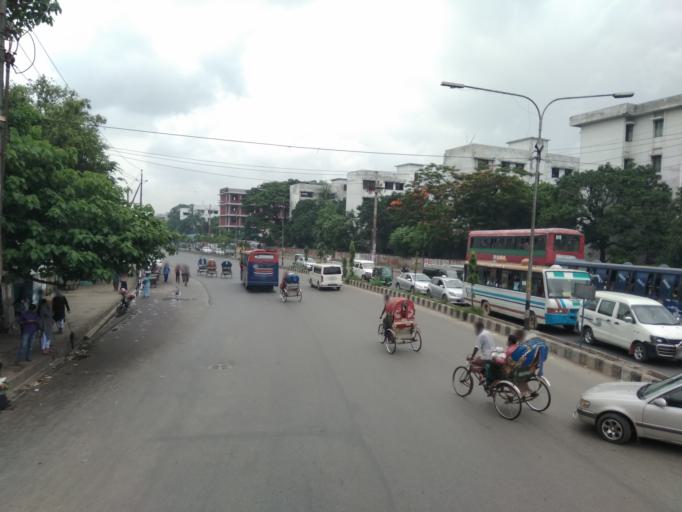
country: BD
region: Dhaka
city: Azimpur
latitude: 23.7851
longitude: 90.3538
